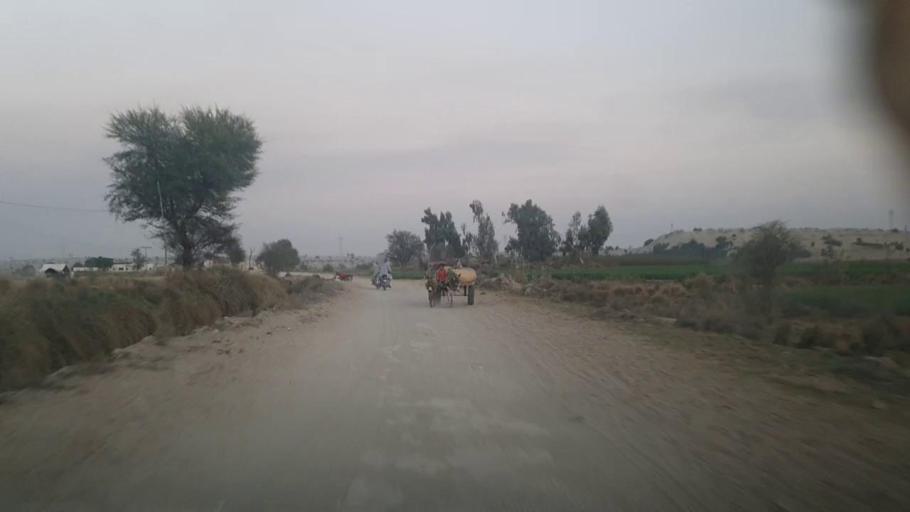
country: PK
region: Sindh
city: Kandiari
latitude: 26.6761
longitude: 68.9568
